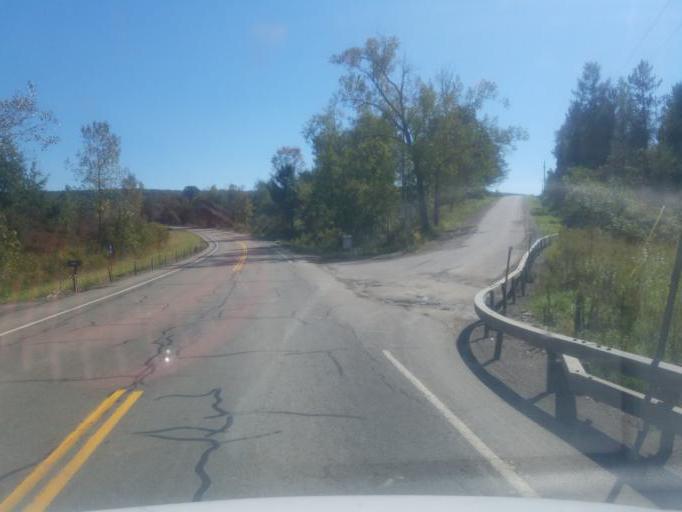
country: US
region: New York
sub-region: Allegany County
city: Friendship
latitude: 42.3024
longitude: -78.1626
